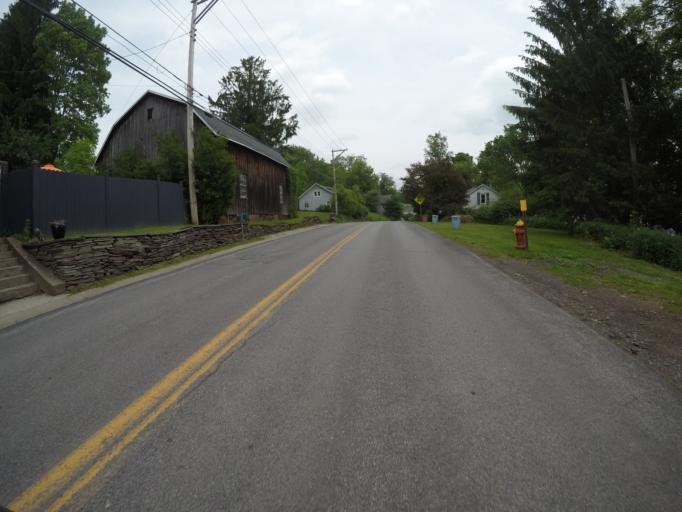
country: US
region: New York
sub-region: Delaware County
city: Delhi
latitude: 42.2614
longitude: -74.7887
